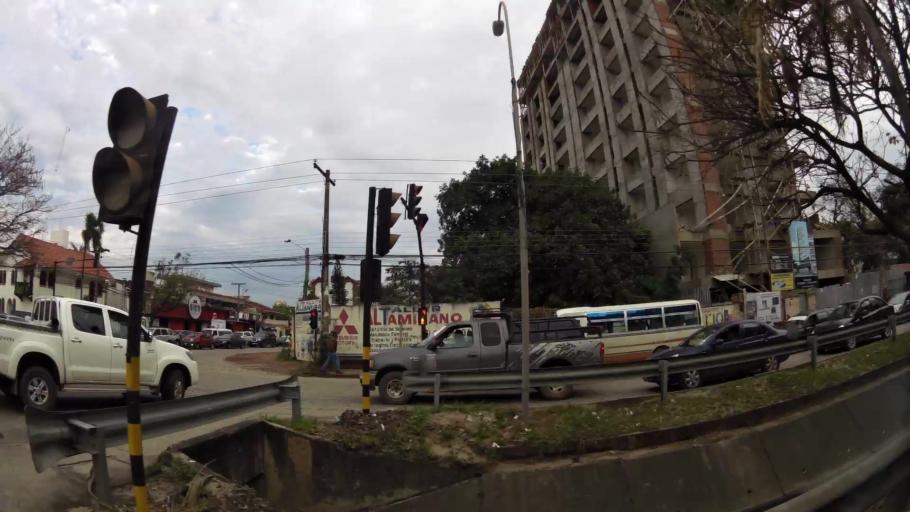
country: BO
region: Santa Cruz
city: Santa Cruz de la Sierra
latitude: -17.7636
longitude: -63.1762
